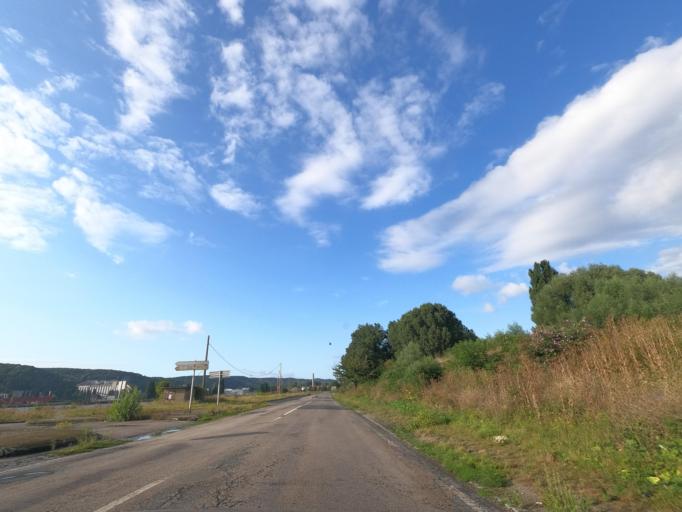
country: FR
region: Haute-Normandie
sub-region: Departement de la Seine-Maritime
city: Petit-Couronne
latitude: 49.3962
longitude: 1.0191
